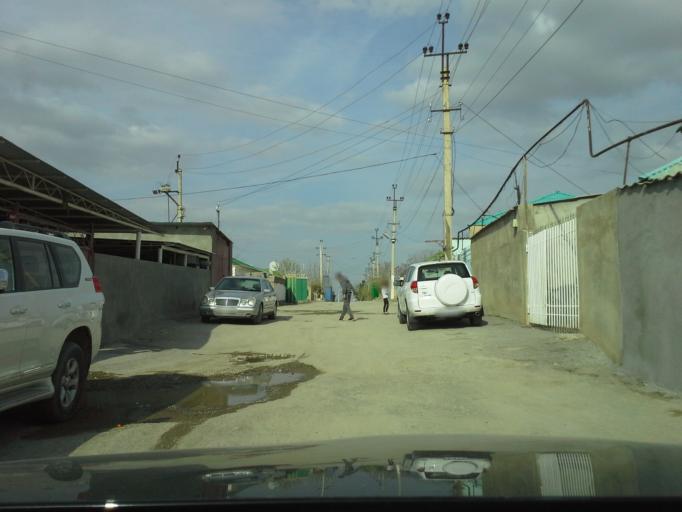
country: TM
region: Ahal
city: Abadan
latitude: 37.9538
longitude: 58.2051
